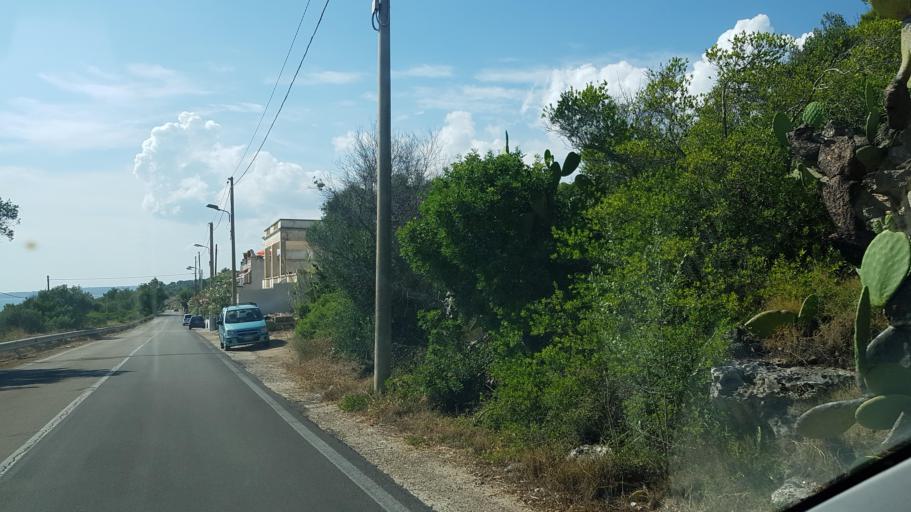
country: IT
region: Apulia
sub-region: Provincia di Lecce
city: Morciano di Leuca
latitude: 39.8156
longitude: 18.3118
